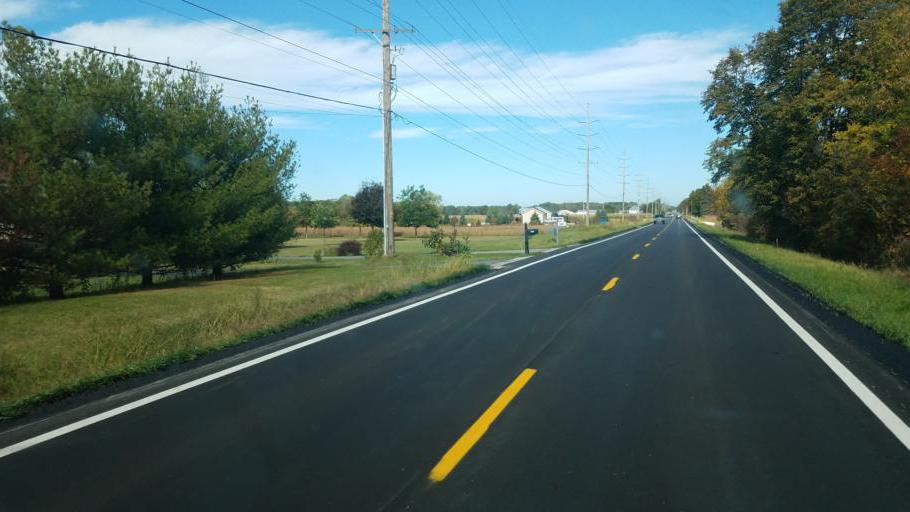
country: US
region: Ohio
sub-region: Erie County
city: Huron
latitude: 41.3412
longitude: -82.4937
